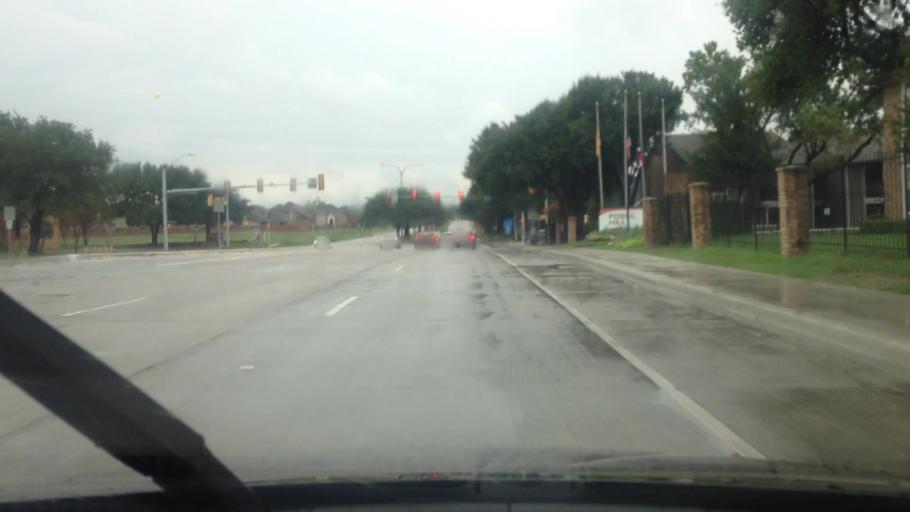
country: US
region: Texas
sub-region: Tarrant County
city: Watauga
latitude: 32.8486
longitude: -97.2899
